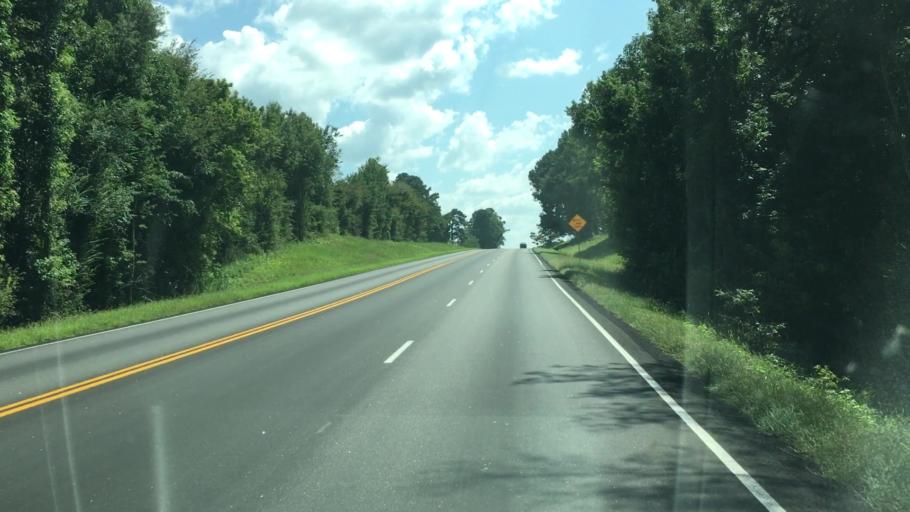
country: US
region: Georgia
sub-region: Morgan County
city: Madison
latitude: 33.6605
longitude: -83.4457
